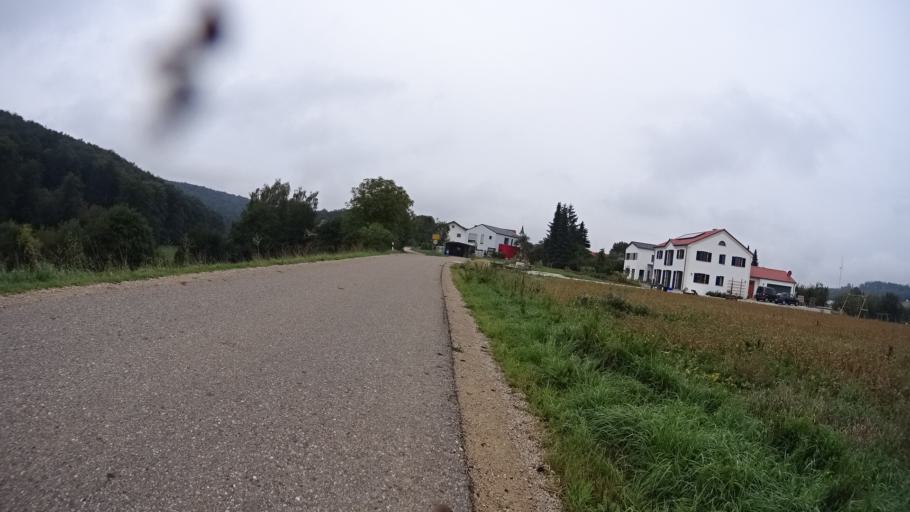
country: DE
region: Bavaria
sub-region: Upper Bavaria
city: Denkendorf
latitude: 48.9204
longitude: 11.4330
